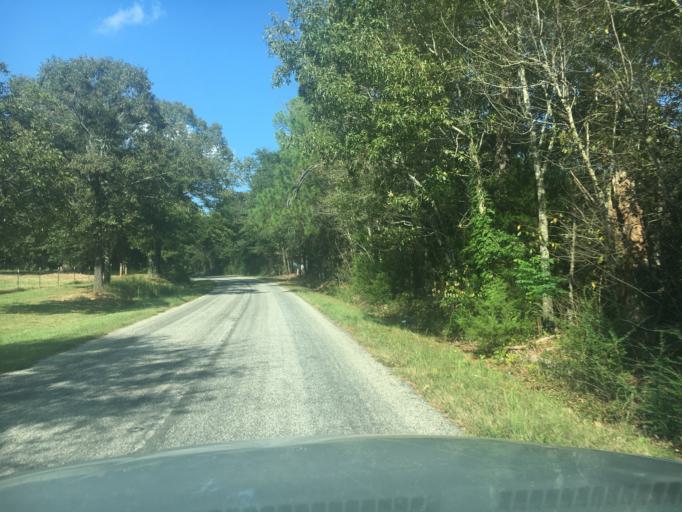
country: US
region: South Carolina
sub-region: Greenwood County
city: Ware Shoals
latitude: 34.4685
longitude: -82.2413
